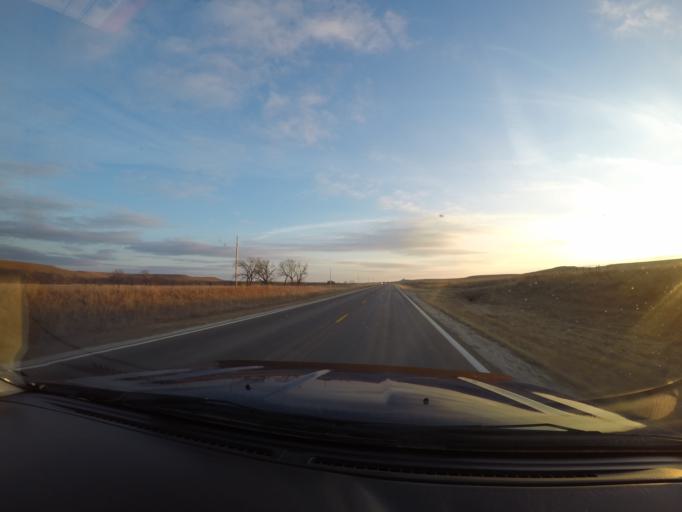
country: US
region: Kansas
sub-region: Chase County
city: Cottonwood Falls
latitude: 38.4275
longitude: -96.5571
